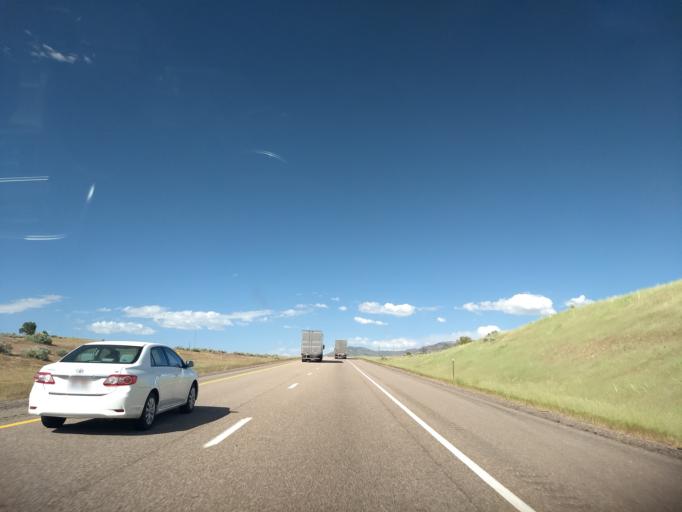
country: US
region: Utah
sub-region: Millard County
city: Fillmore
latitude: 39.0907
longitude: -112.2682
